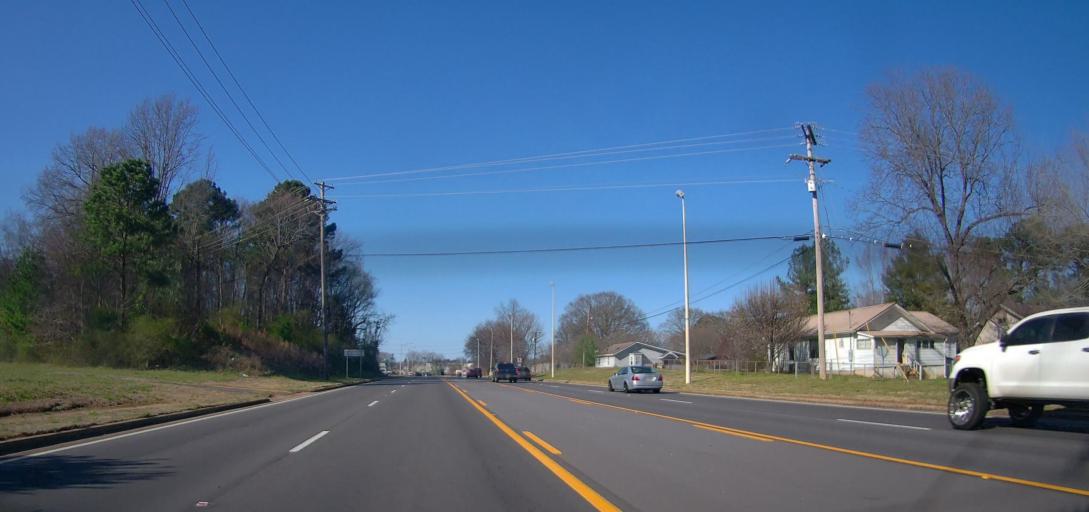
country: US
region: Alabama
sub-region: Lauderdale County
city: East Florence
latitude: 34.8203
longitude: -87.6265
